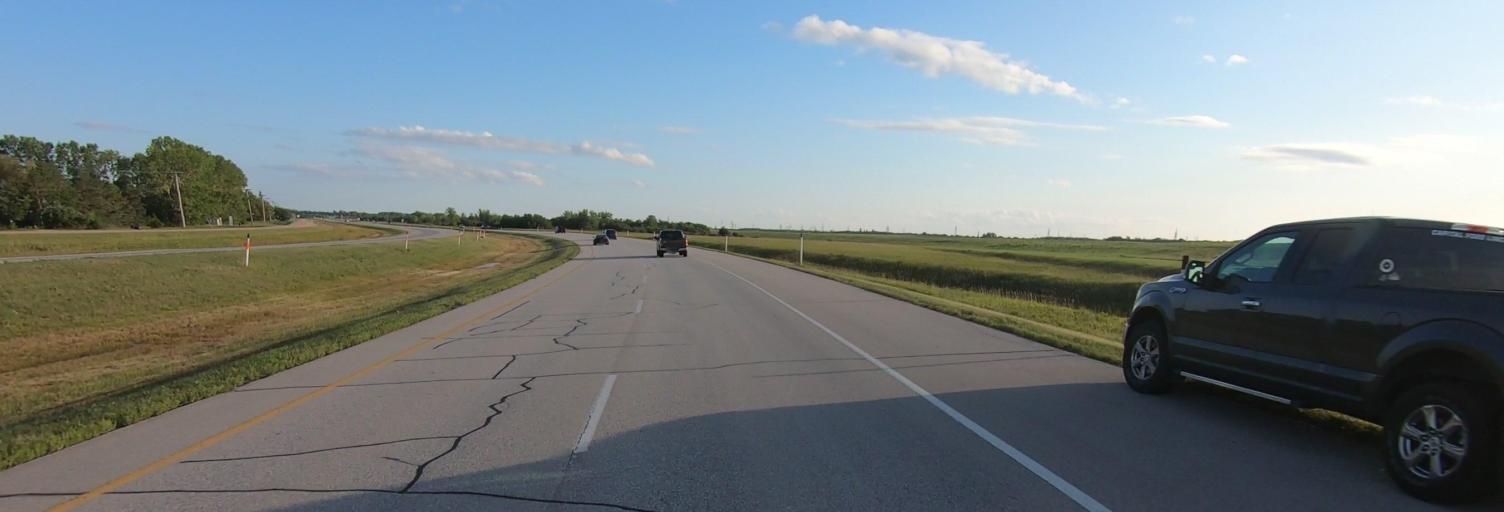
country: CA
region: Manitoba
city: Selkirk
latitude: 49.9910
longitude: -96.9770
